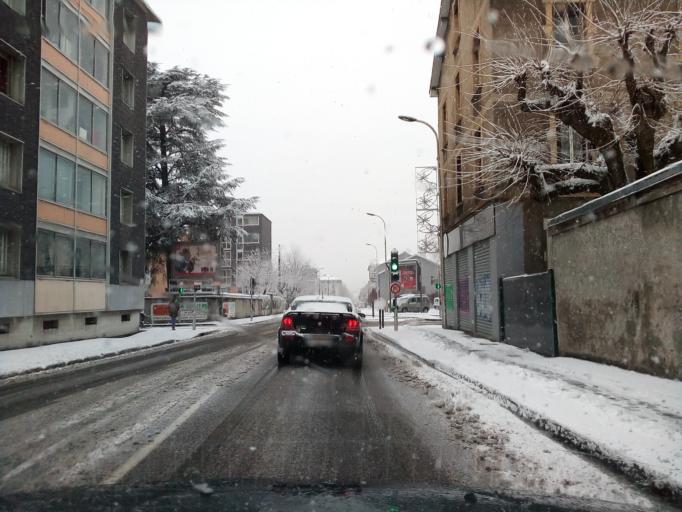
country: FR
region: Rhone-Alpes
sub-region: Departement de l'Isere
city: Saint-Martin-d'Heres
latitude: 45.1831
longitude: 5.7572
